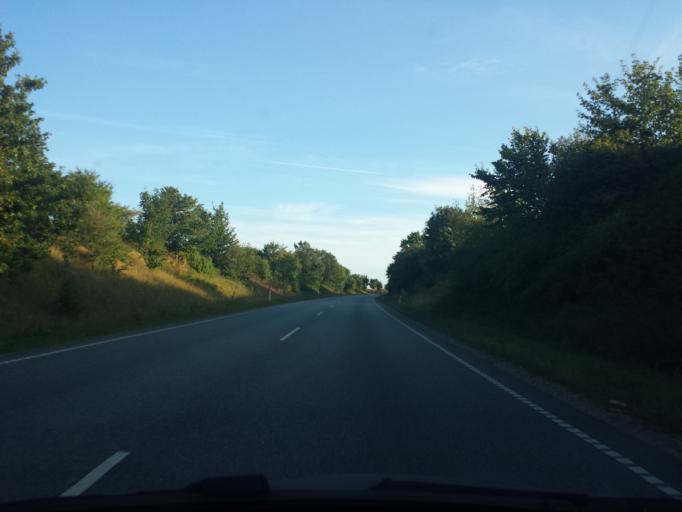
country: DK
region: Capital Region
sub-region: Frederikssund Kommune
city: Frederikssund
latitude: 55.8225
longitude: 12.1052
